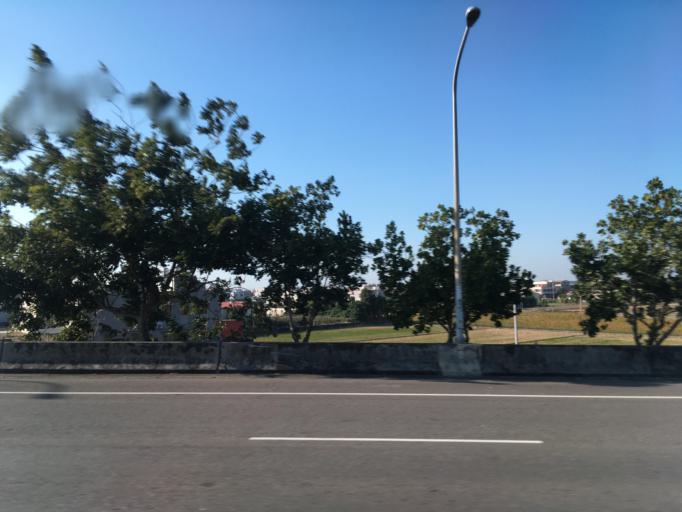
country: TW
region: Taiwan
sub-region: Chiayi
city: Taibao
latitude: 23.4297
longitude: 120.3191
